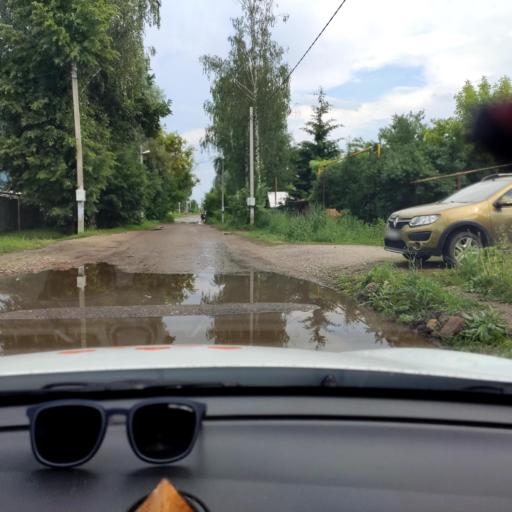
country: RU
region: Tatarstan
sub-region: Zelenodol'skiy Rayon
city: Vasil'yevo
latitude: 55.8289
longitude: 48.7110
